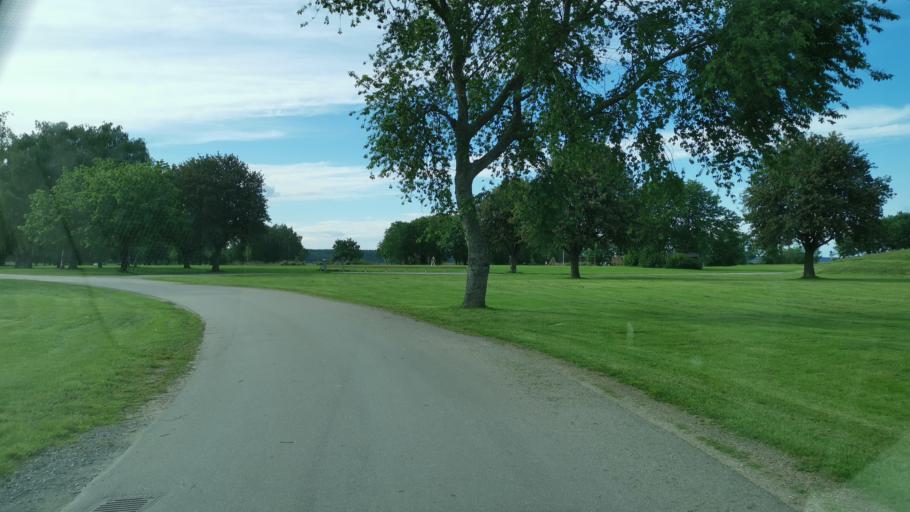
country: SE
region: Vaestra Goetaland
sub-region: Vanersborgs Kommun
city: Vanersborg
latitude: 58.3814
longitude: 12.3381
